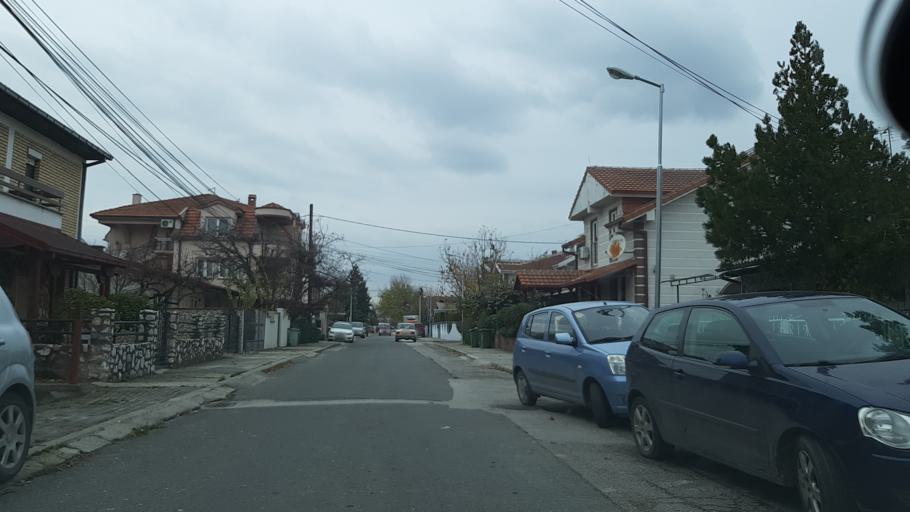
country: MK
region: Kisela Voda
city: Usje
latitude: 41.9710
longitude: 21.4743
